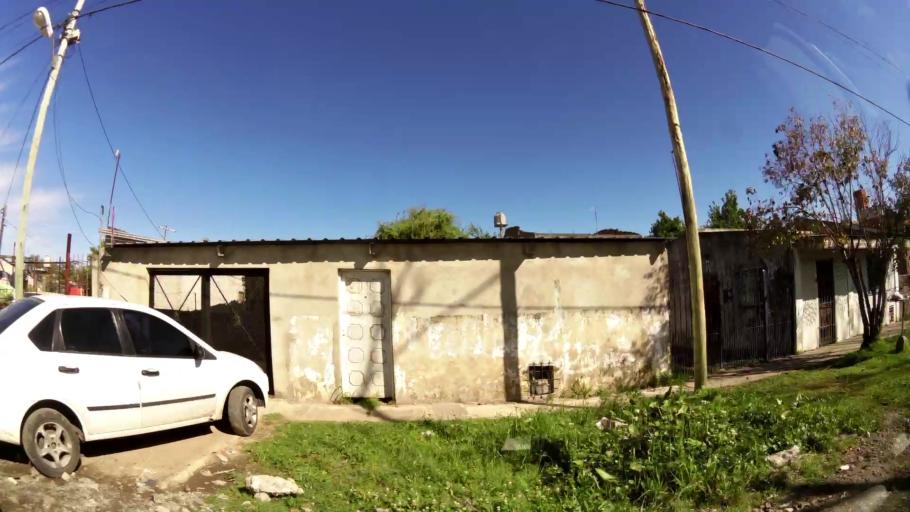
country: AR
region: Buenos Aires
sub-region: Partido de Quilmes
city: Quilmes
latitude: -34.7629
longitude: -58.3089
